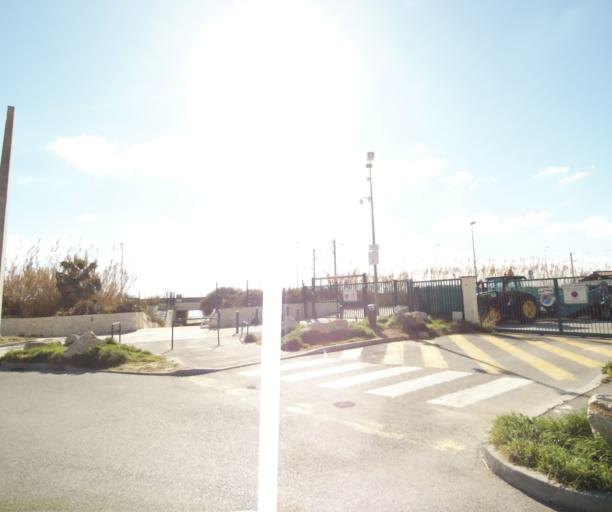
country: FR
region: Provence-Alpes-Cote d'Azur
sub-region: Departement des Alpes-Maritimes
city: Antibes
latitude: 43.5717
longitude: 7.0964
